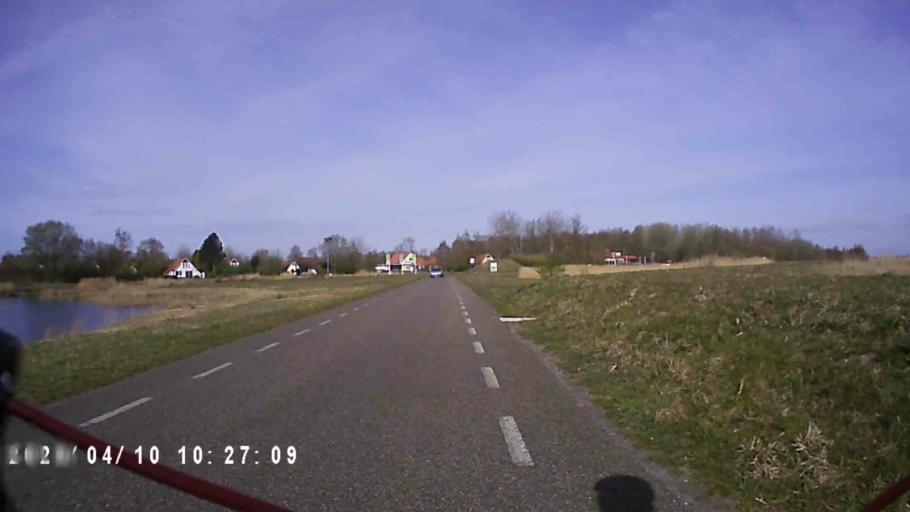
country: NL
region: Friesland
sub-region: Gemeente Dongeradeel
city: Anjum
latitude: 53.3889
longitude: 6.2181
